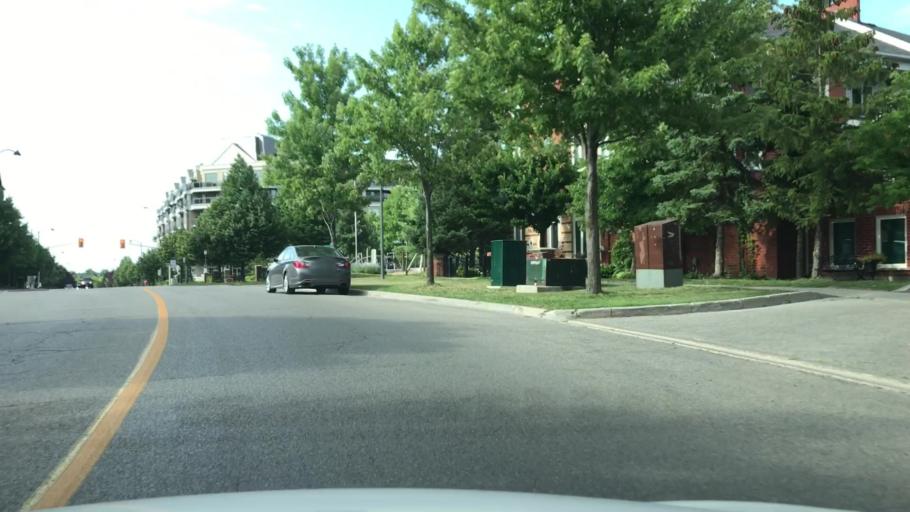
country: CA
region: Ontario
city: Newmarket
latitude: 44.0071
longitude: -79.4496
